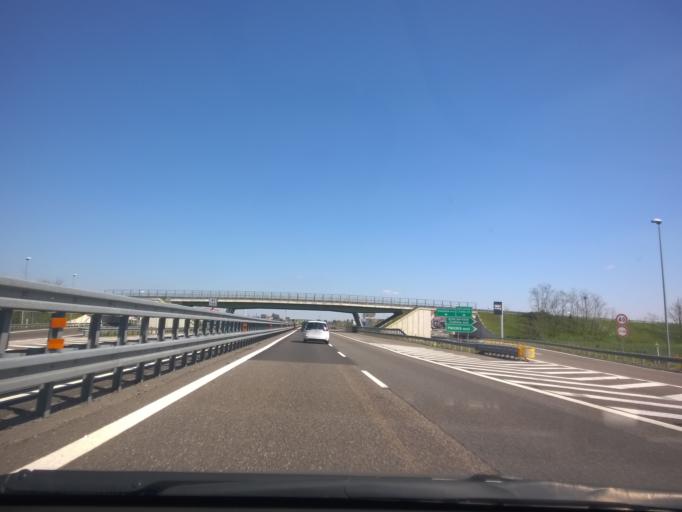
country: IT
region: Emilia-Romagna
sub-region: Provincia di Piacenza
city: San Nicolo
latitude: 45.0616
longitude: 9.6499
